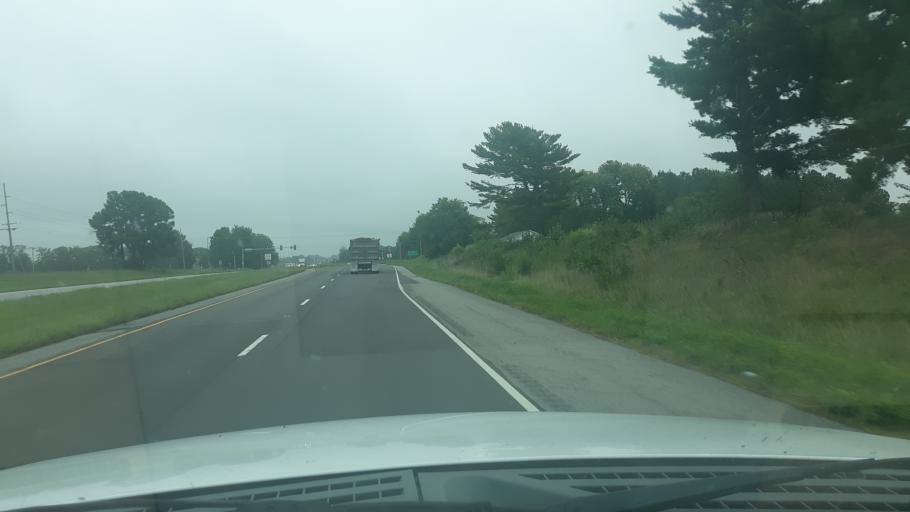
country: US
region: Illinois
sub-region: Williamson County
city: Marion
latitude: 37.7284
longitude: -88.8576
